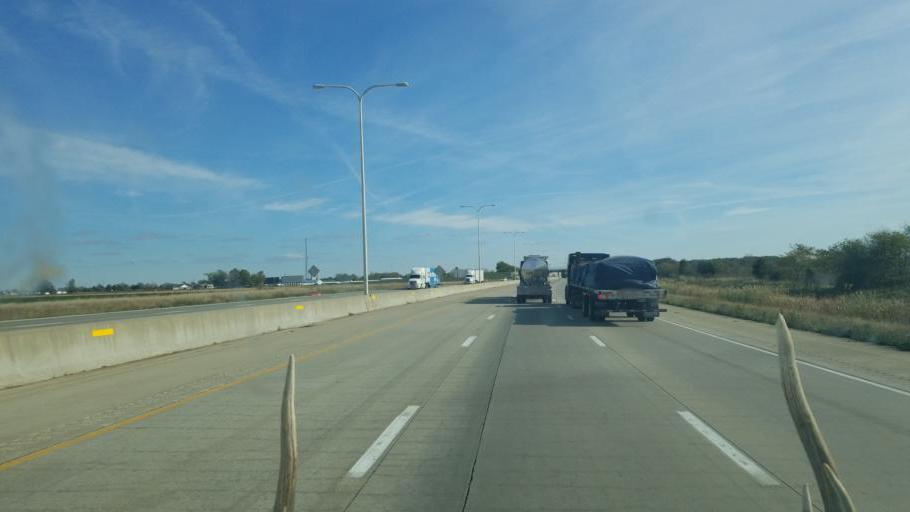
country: US
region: Illinois
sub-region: Effingham County
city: Effingham
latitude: 39.1425
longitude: -88.5493
